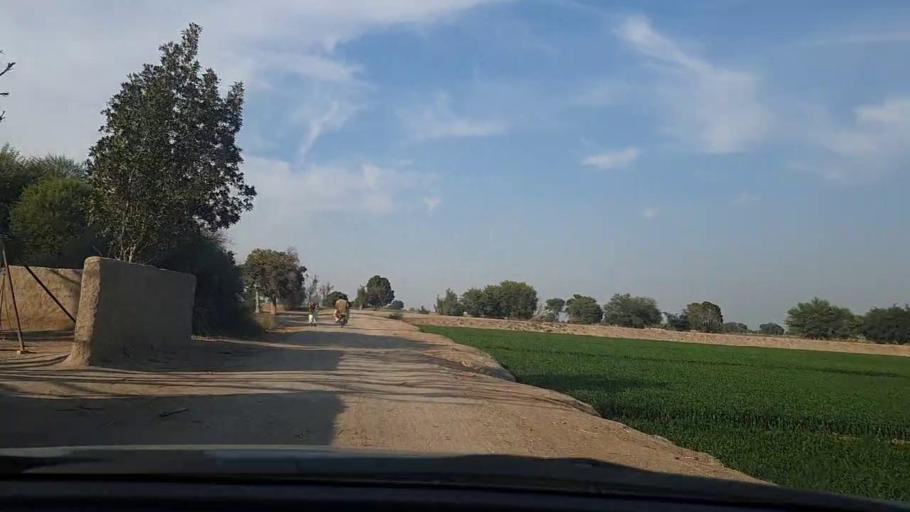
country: PK
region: Sindh
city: Daulatpur
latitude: 26.3202
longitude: 68.0202
